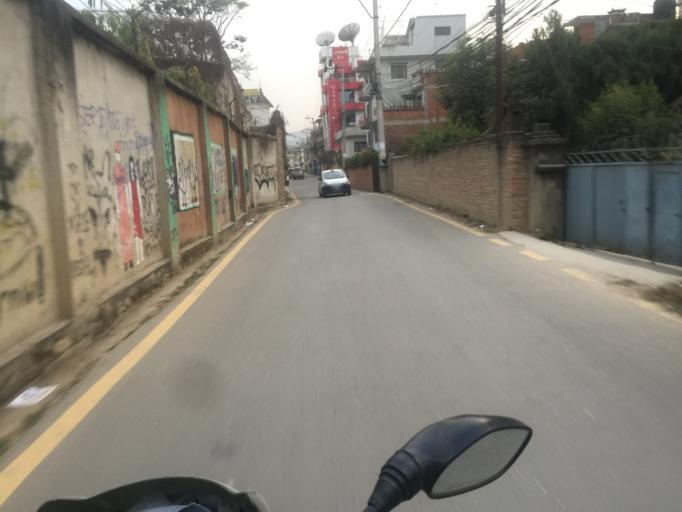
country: NP
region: Central Region
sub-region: Bagmati Zone
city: Patan
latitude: 27.6737
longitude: 85.3095
